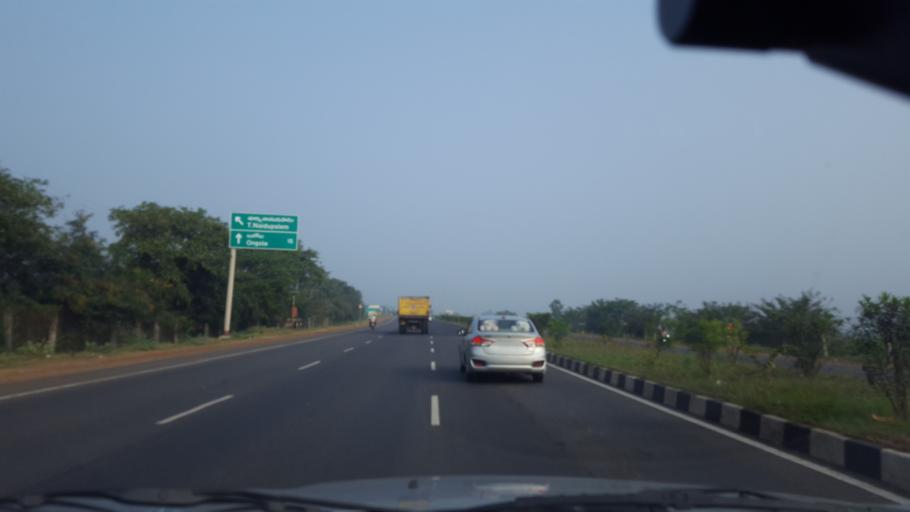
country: IN
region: Andhra Pradesh
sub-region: Prakasam
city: Ongole
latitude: 15.3842
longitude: 80.0401
